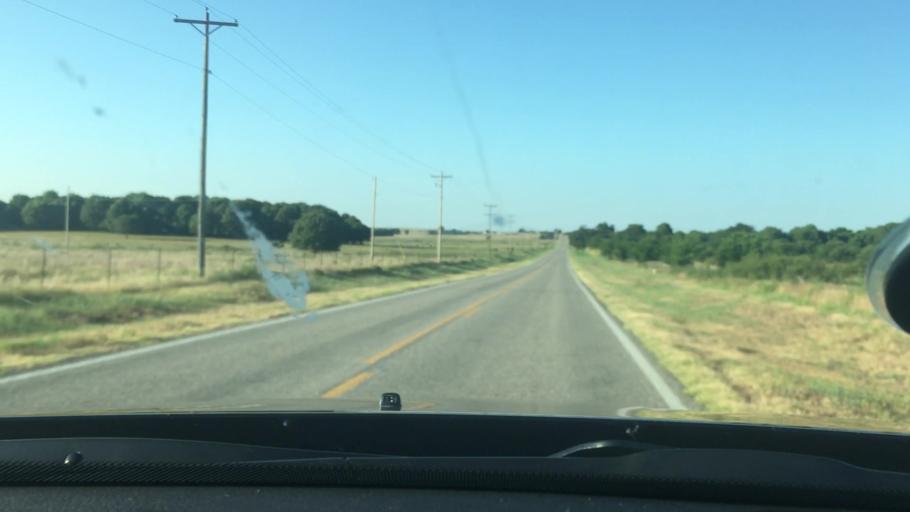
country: US
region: Oklahoma
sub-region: Murray County
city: Sulphur
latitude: 34.5726
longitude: -96.8448
